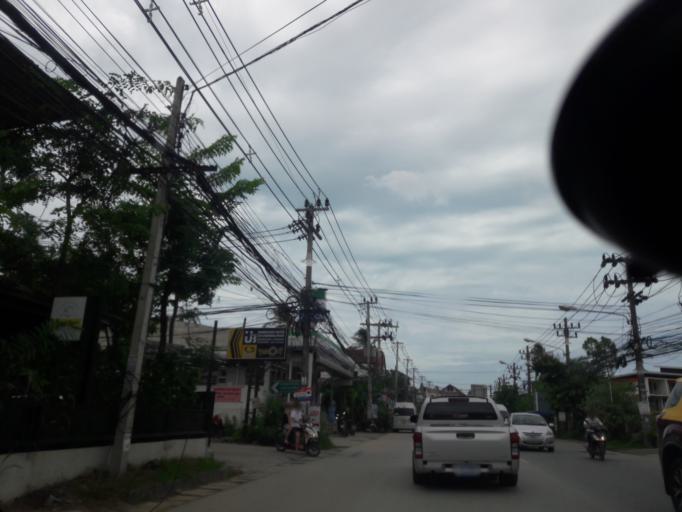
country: TH
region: Surat Thani
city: Ko Samui
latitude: 9.5544
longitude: 100.0324
